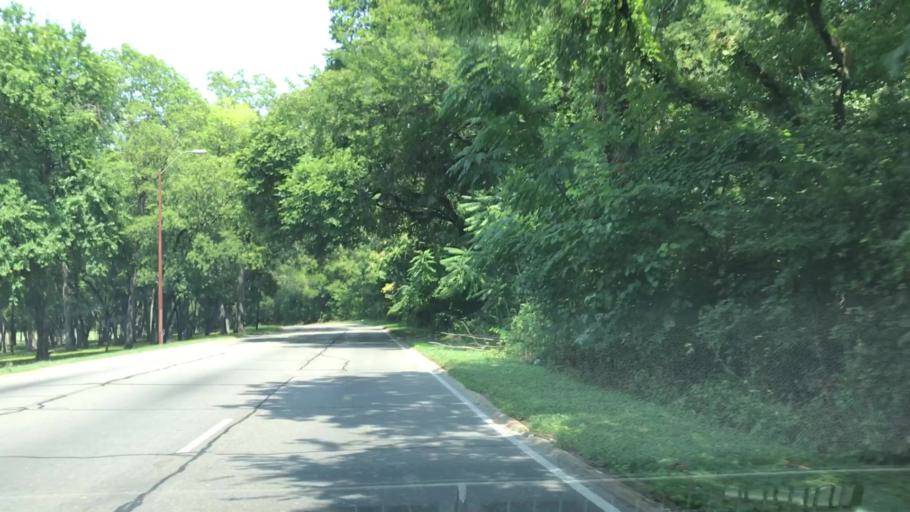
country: US
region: Texas
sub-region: Dallas County
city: Highland Park
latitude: 32.7996
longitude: -96.7392
